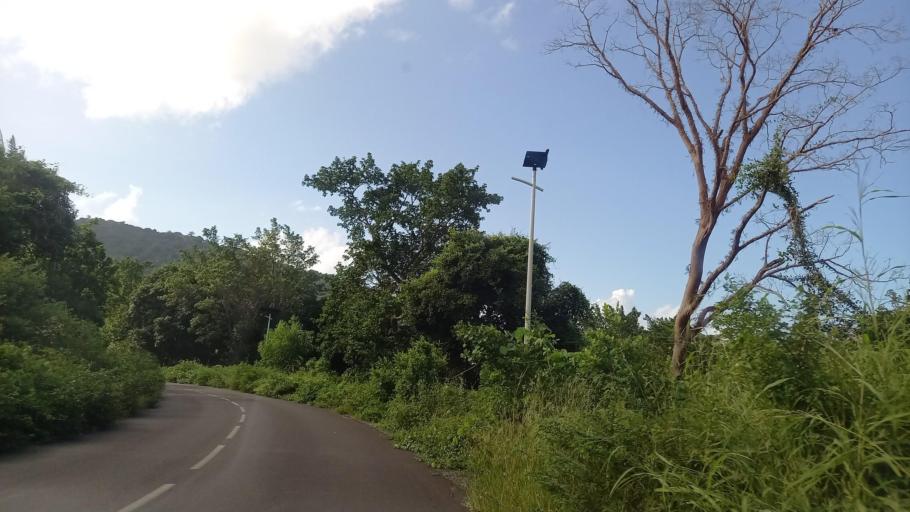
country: YT
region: Kani-Keli
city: Kani Keli
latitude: -12.9861
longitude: 45.1335
